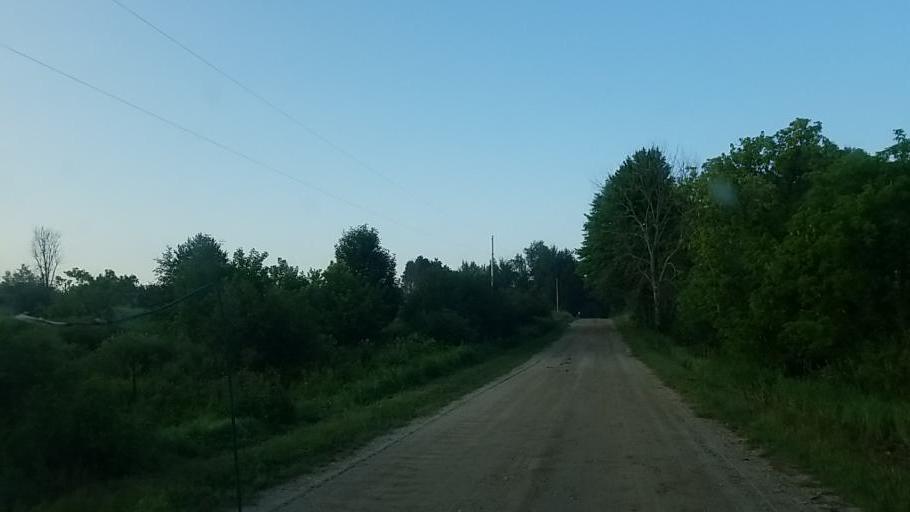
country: US
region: Michigan
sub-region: Osceola County
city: Evart
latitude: 43.9031
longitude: -85.1677
